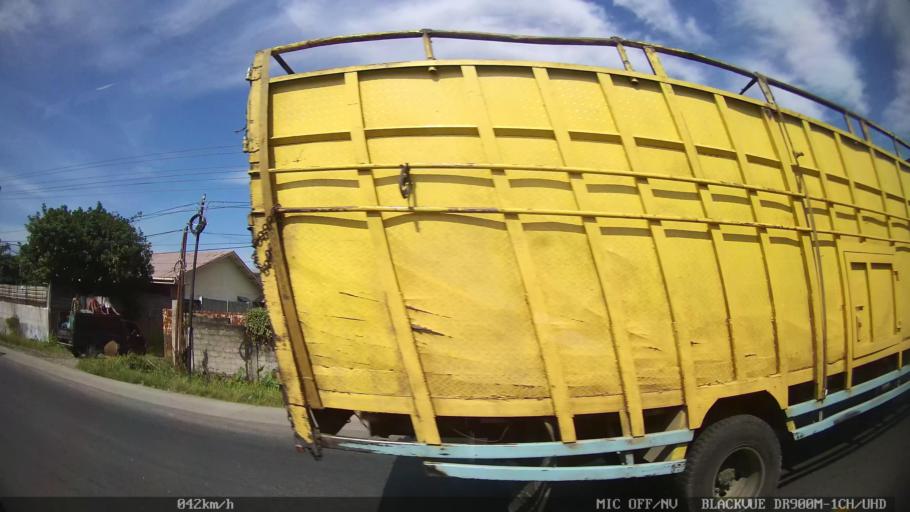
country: ID
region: North Sumatra
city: Binjai
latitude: 3.6764
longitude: 98.5093
